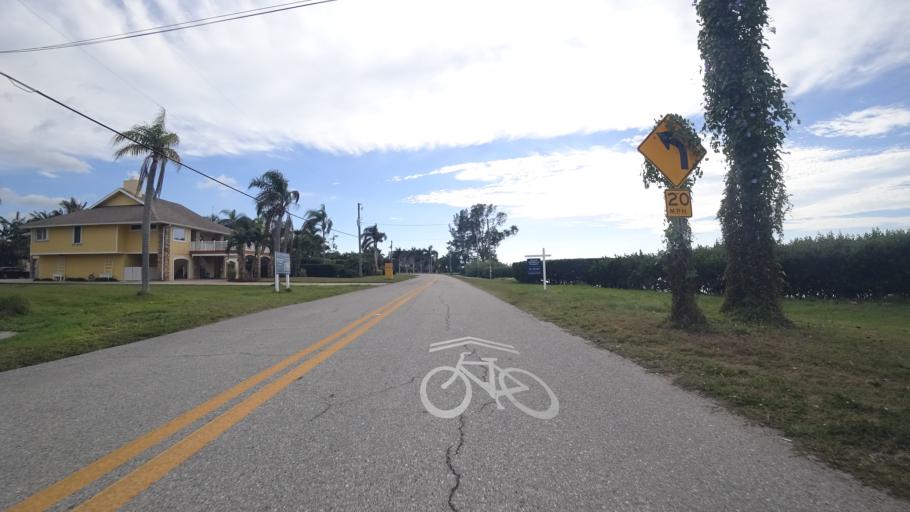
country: US
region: Florida
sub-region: Manatee County
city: West Bradenton
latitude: 27.4850
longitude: -82.6445
